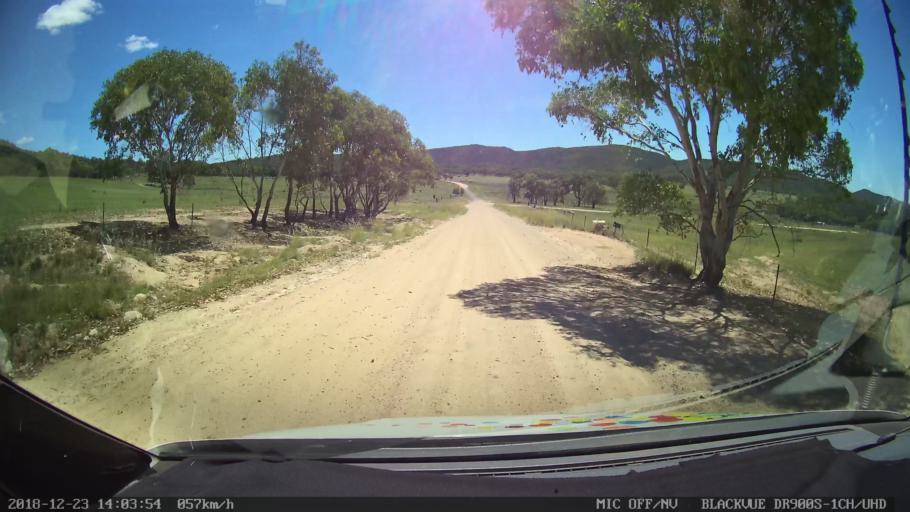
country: AU
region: New South Wales
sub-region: Tamworth Municipality
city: Manilla
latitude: -30.6224
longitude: 151.0960
